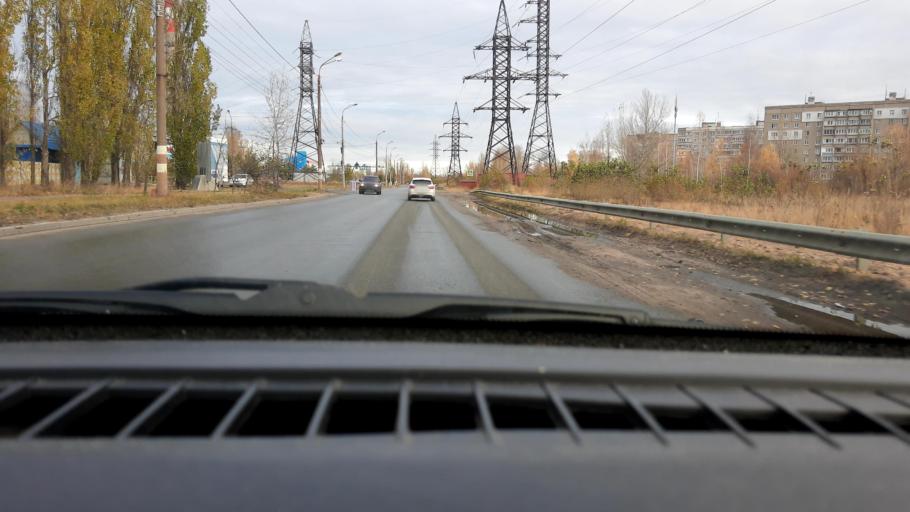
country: RU
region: Nizjnij Novgorod
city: Gorbatovka
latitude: 56.3685
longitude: 43.7970
